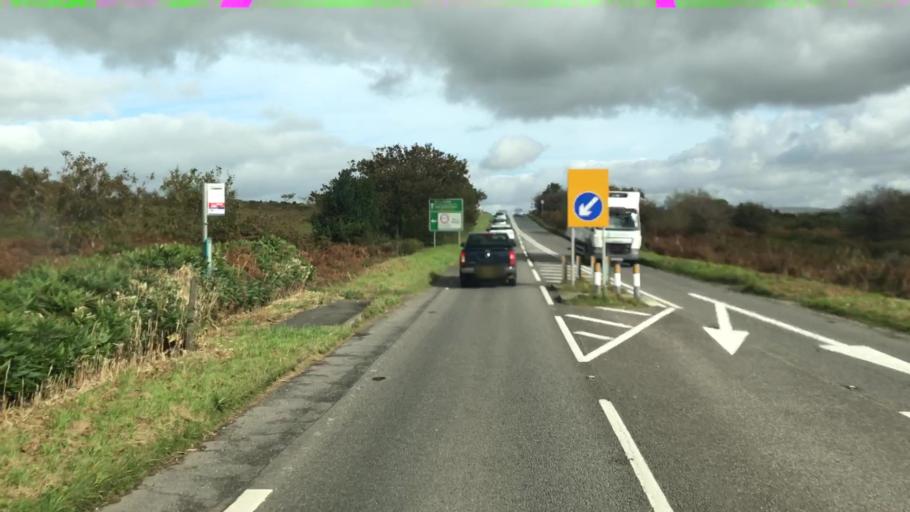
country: GB
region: England
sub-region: Devon
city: Yelverton
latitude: 50.4558
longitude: -4.1054
